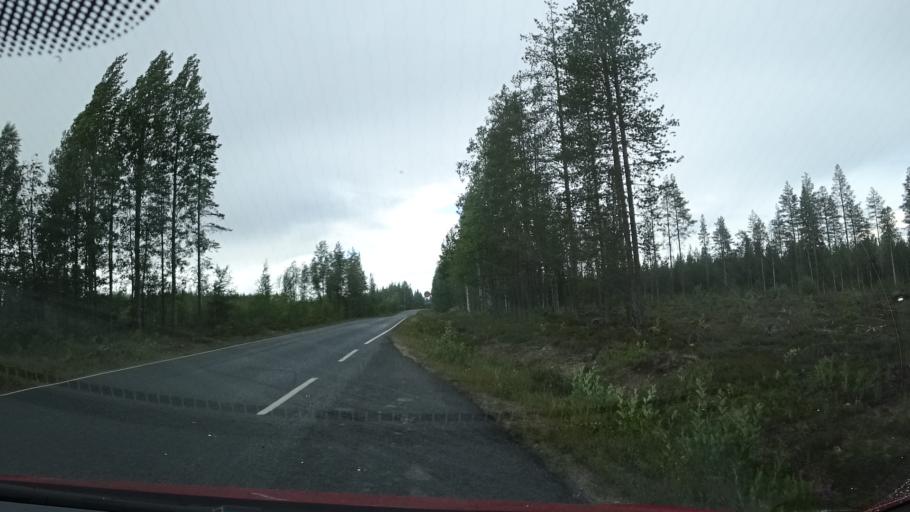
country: FI
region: Kainuu
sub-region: Kehys-Kainuu
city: Kuhmo
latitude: 63.9802
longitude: 29.2626
